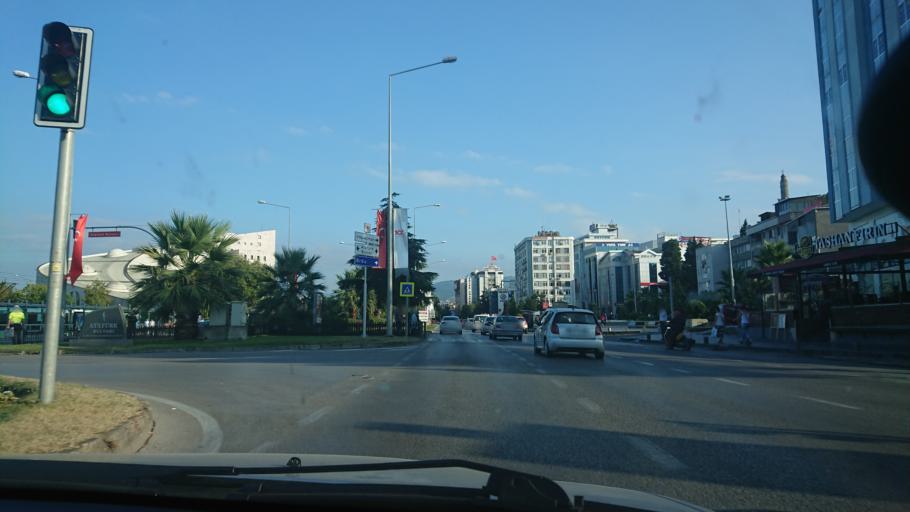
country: TR
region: Samsun
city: Samsun
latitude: 41.2959
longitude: 36.3330
